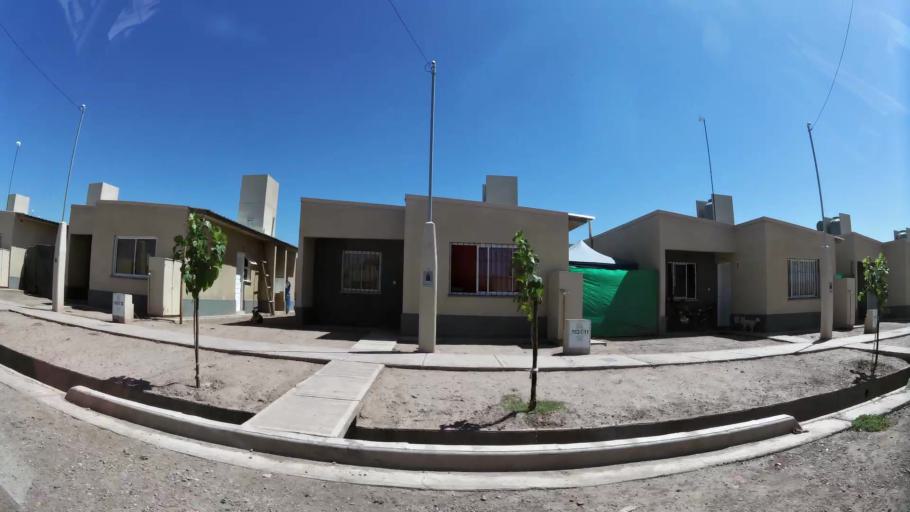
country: AR
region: Mendoza
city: Villa Nueva
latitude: -32.8748
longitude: -68.7889
